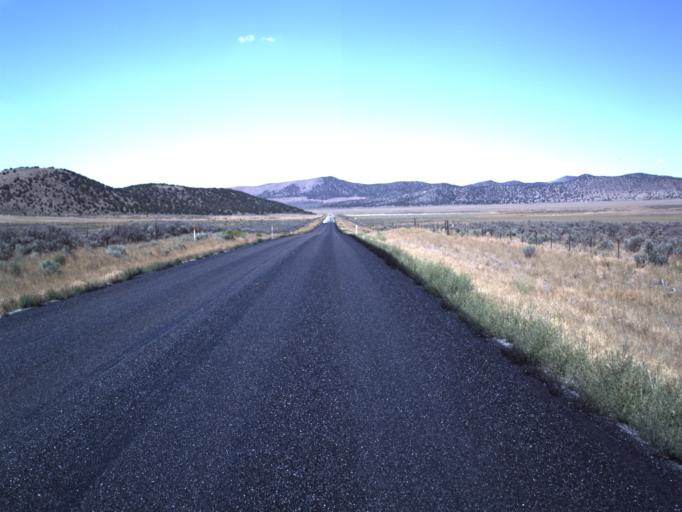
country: US
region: Utah
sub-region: Juab County
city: Nephi
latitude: 39.6976
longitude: -111.9599
